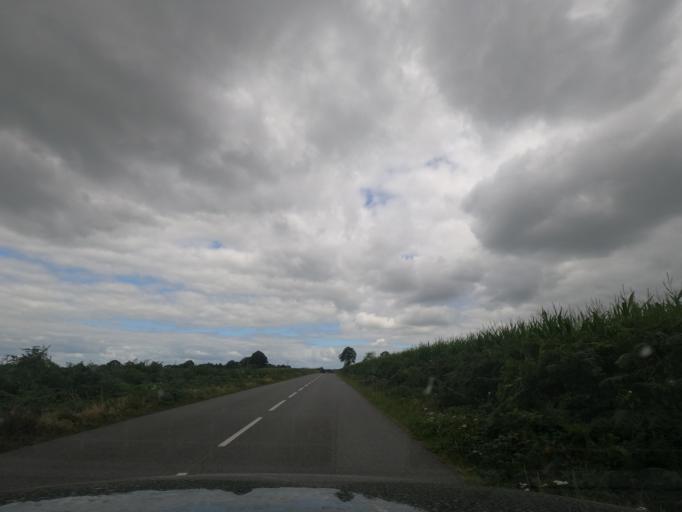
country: FR
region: Brittany
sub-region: Departement d'Ille-et-Vilaine
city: Landean
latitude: 48.4250
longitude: -1.1247
